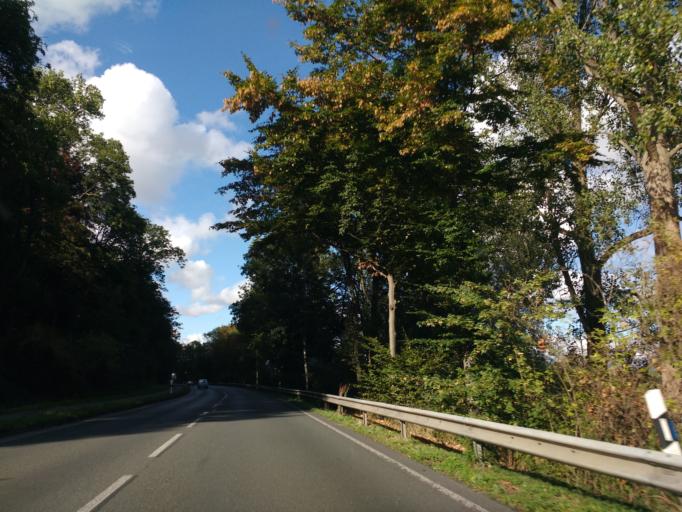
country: DE
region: North Rhine-Westphalia
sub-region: Regierungsbezirk Dusseldorf
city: Xanten
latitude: 51.6465
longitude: 6.4770
